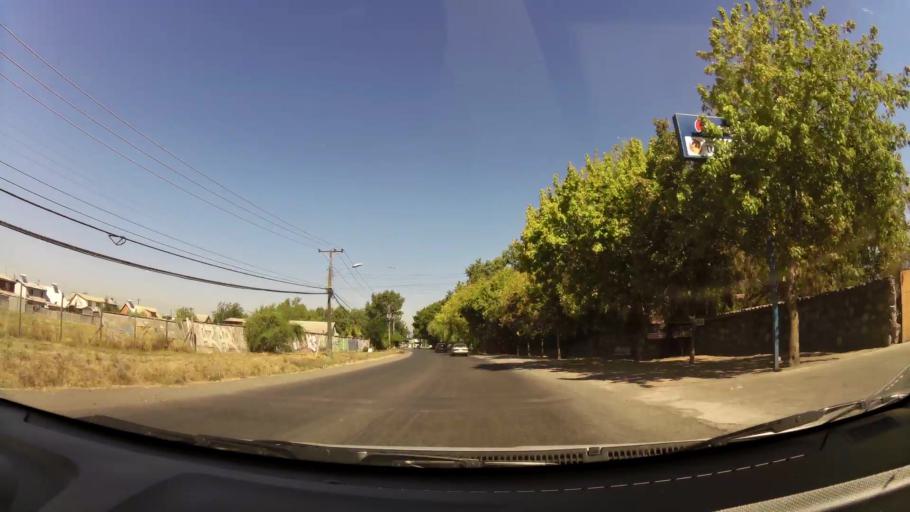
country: CL
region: Maule
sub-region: Provincia de Curico
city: Curico
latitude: -34.9756
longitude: -71.2589
